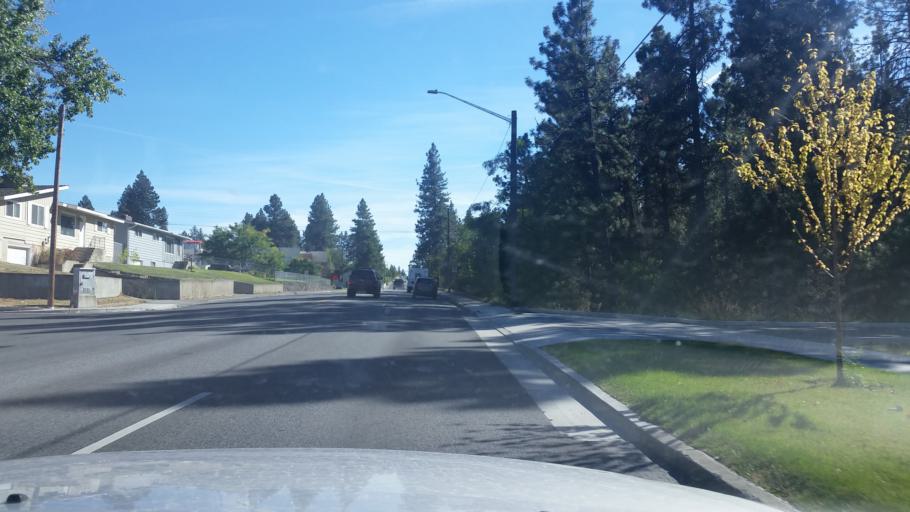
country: US
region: Washington
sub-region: Spokane County
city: Spokane
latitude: 47.6358
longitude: -117.3632
